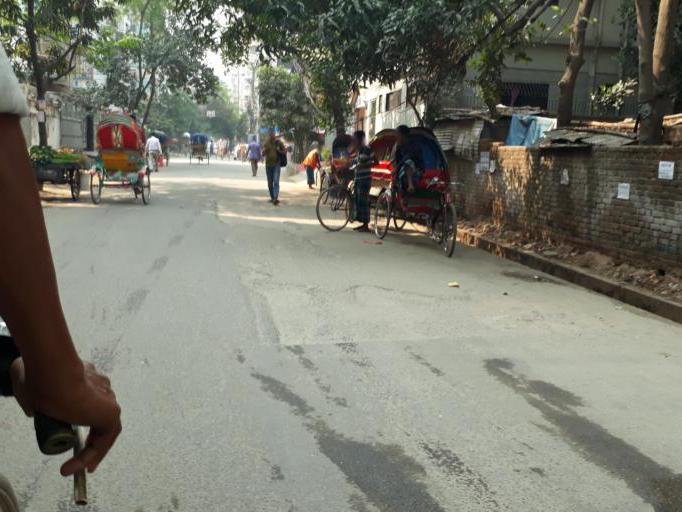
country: BD
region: Dhaka
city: Tungi
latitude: 23.8786
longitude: 90.3901
